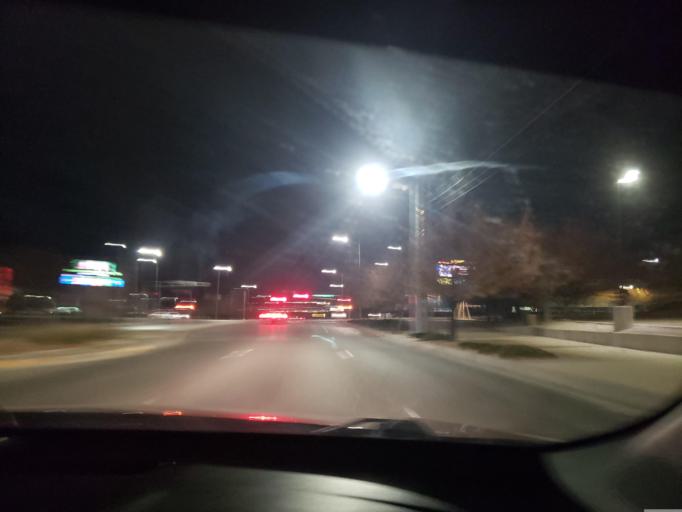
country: US
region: New Mexico
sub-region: Bernalillo County
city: Albuquerque
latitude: 35.0685
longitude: -106.6297
